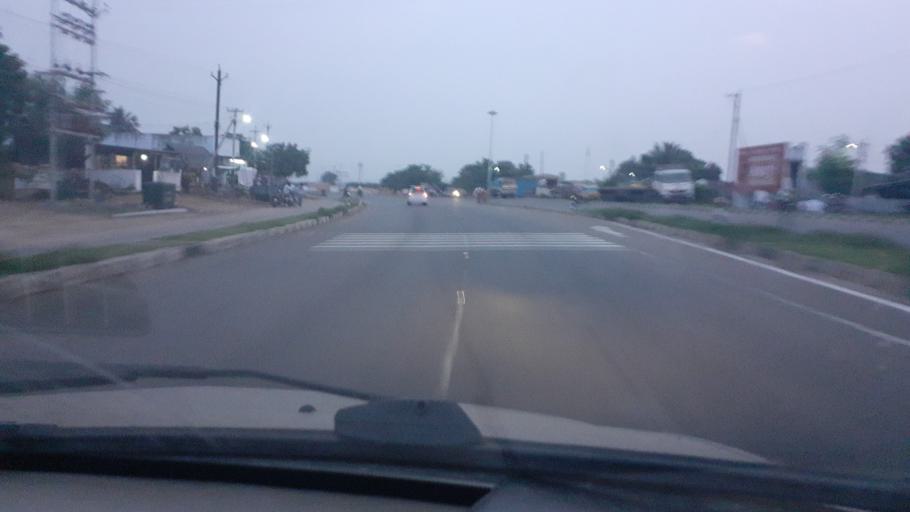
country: IN
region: Tamil Nadu
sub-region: Thoothukkudi
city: Srivaikuntam
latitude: 8.7112
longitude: 77.8232
